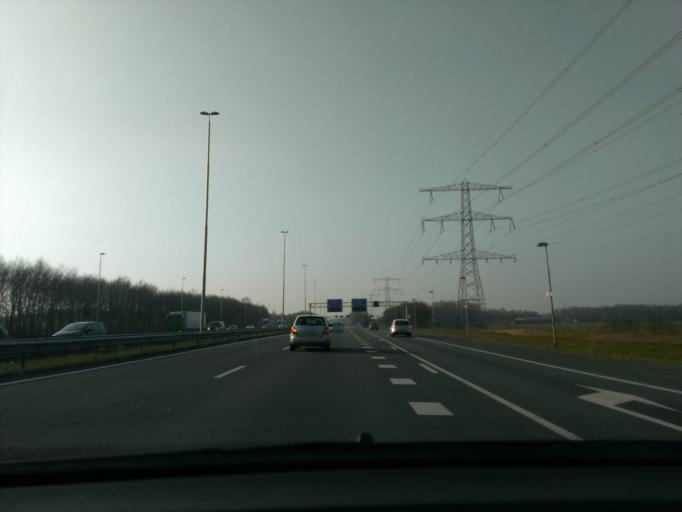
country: NL
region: Overijssel
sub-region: Gemeente Borne
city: Borne
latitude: 52.3058
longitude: 6.7089
